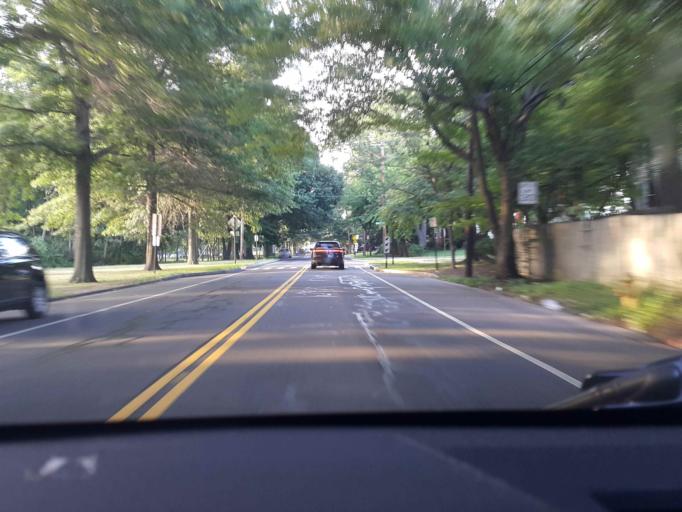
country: US
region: Connecticut
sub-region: New Haven County
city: East Haven
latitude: 41.2760
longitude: -72.8994
